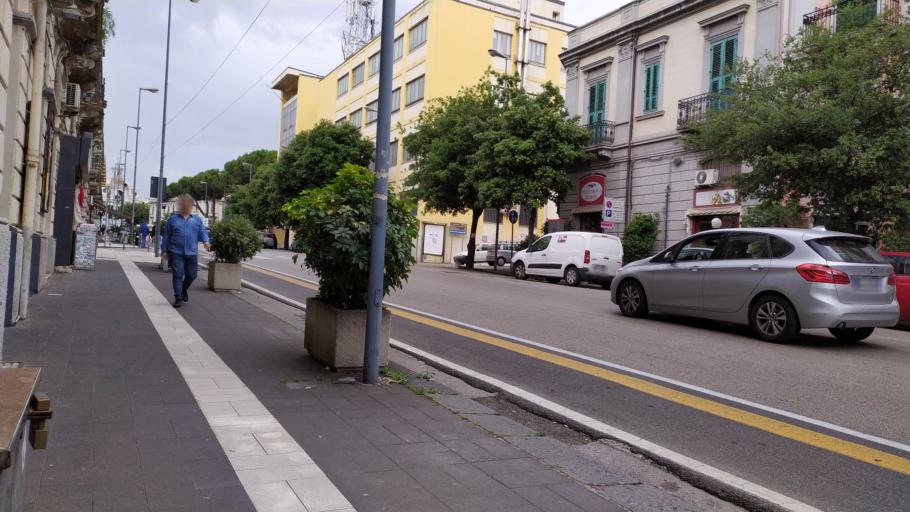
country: IT
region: Sicily
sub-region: Messina
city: Messina
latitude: 38.1908
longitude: 15.5525
